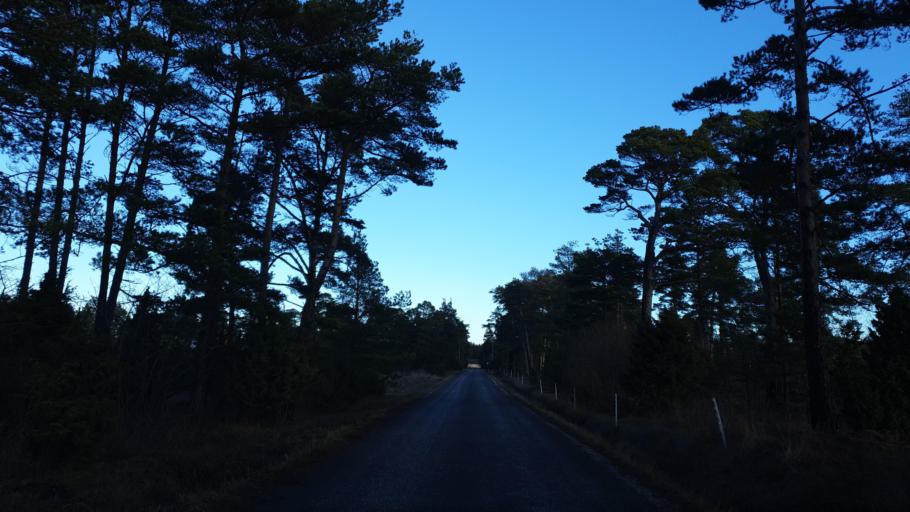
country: SE
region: Gotland
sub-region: Gotland
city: Slite
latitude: 57.3803
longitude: 18.8055
